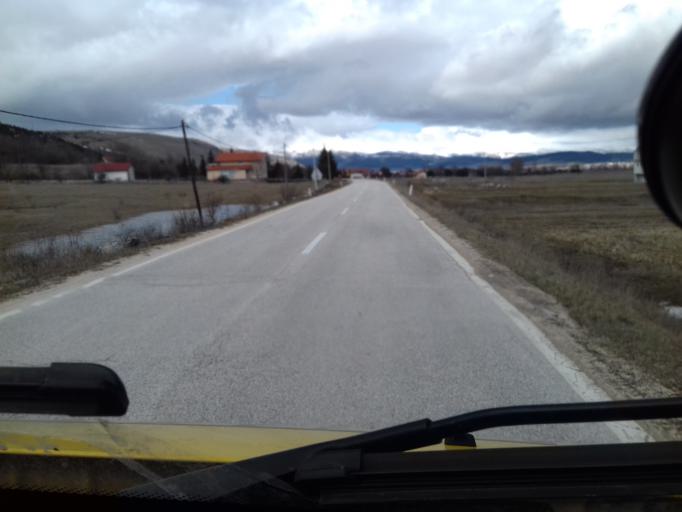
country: BA
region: Federation of Bosnia and Herzegovina
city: Tomislavgrad
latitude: 43.6325
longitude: 17.2449
